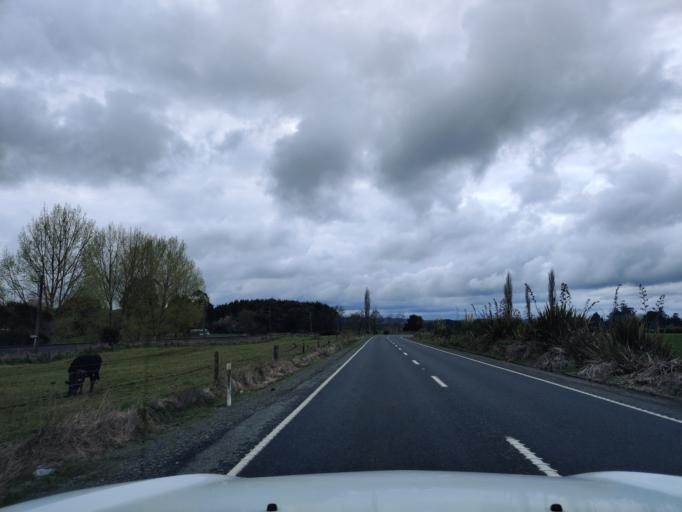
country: NZ
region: Waikato
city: Turangi
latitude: -39.0242
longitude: 175.3808
